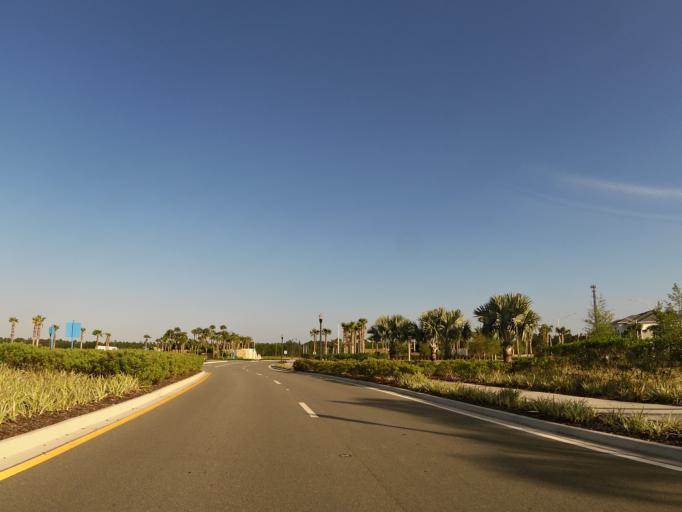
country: US
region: Florida
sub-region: Saint Johns County
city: Palm Valley
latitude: 30.0780
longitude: -81.4861
